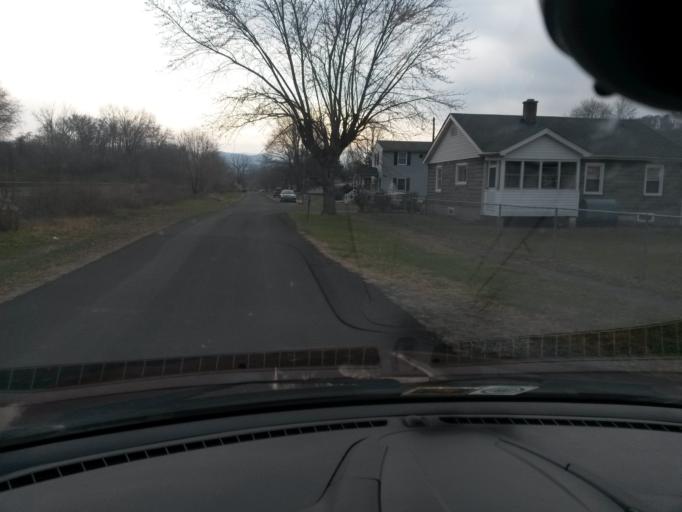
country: US
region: Virginia
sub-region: Alleghany County
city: Clifton Forge
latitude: 37.8011
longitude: -79.7916
